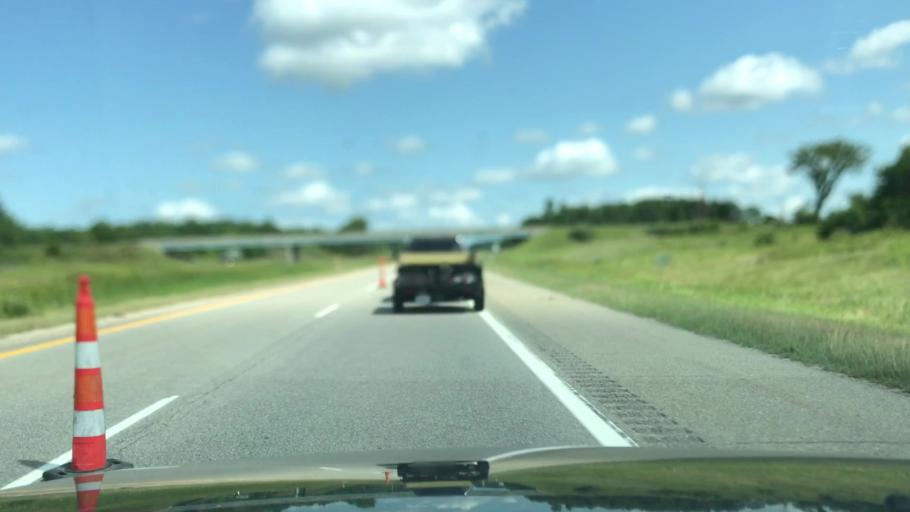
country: US
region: Michigan
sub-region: Mecosta County
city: Big Rapids
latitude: 43.7695
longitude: -85.5346
